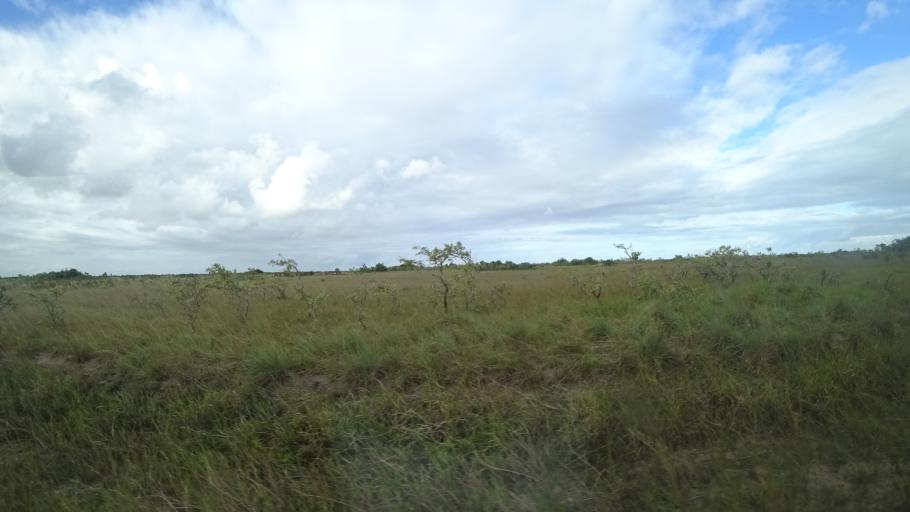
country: MZ
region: Sofala
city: Beira
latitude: -19.6728
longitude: 35.0589
